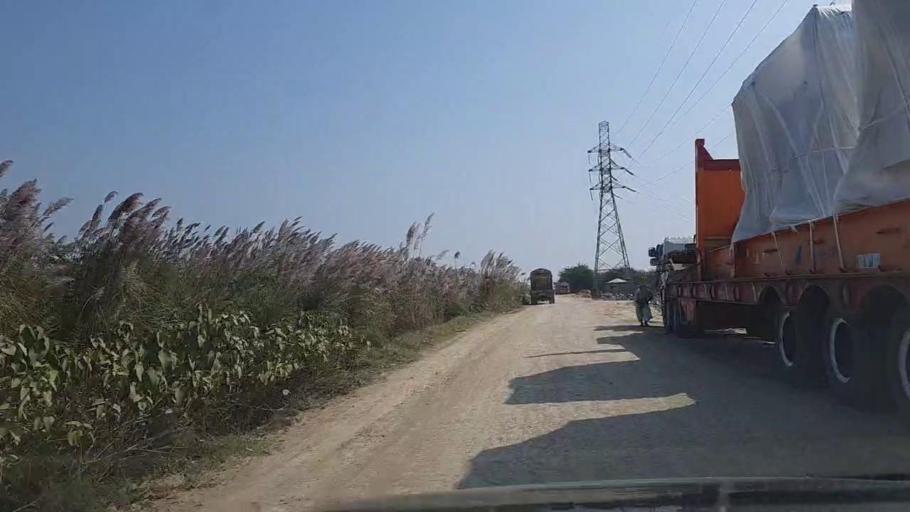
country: PK
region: Sindh
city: Gharo
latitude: 24.7212
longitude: 67.5557
